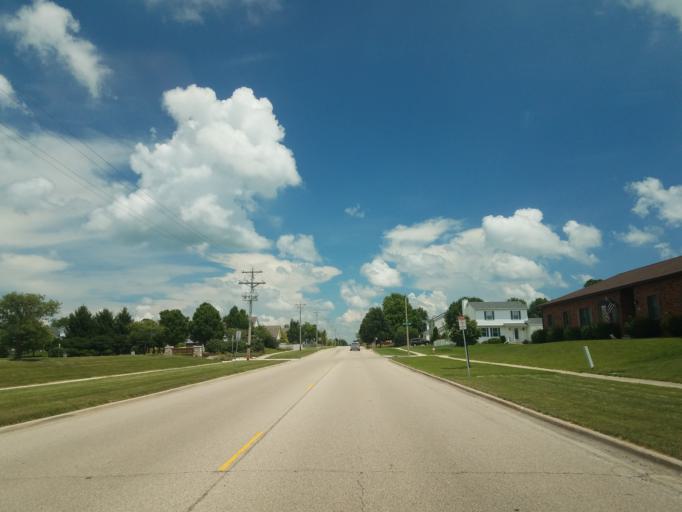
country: US
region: Illinois
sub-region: McLean County
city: Normal
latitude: 40.4958
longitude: -88.9350
